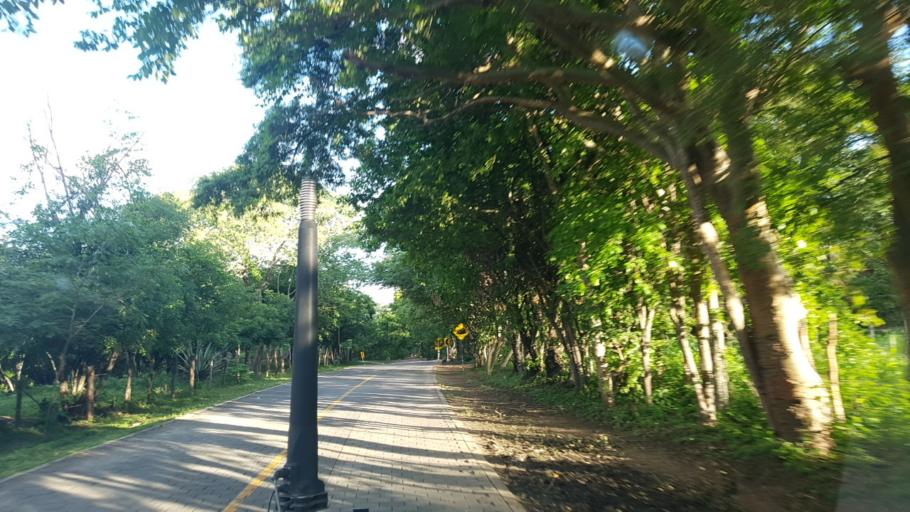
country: NI
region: Nueva Segovia
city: Ocotal
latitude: 13.6414
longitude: -86.5914
